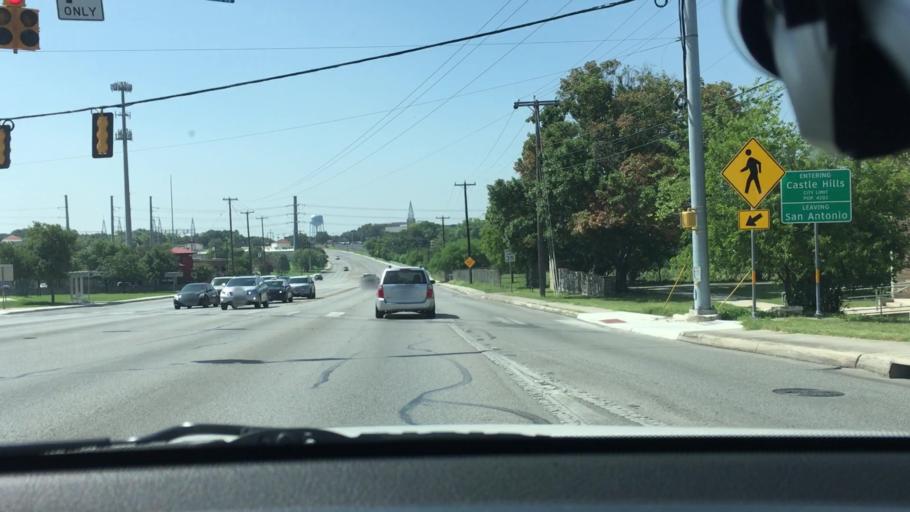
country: US
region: Texas
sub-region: Bexar County
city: Castle Hills
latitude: 29.5407
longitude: -98.5277
